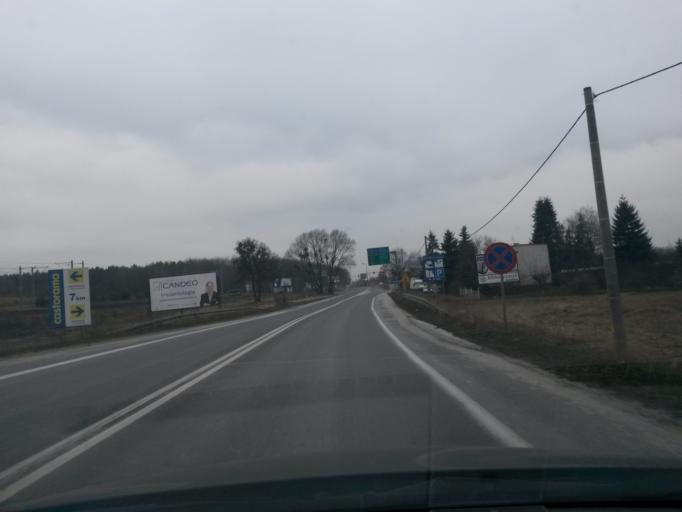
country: PL
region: Greater Poland Voivodeship
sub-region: Powiat poznanski
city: Czerwonak
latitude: 52.4310
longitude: 17.0136
